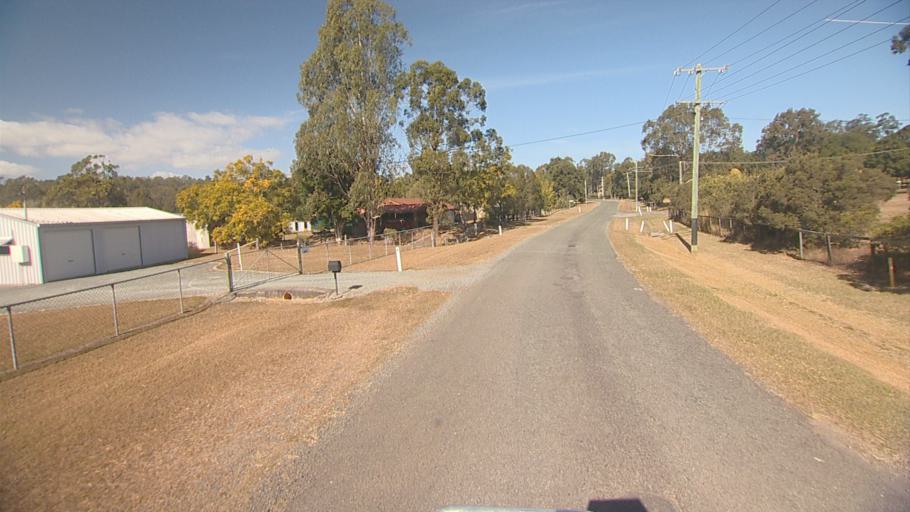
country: AU
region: Queensland
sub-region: Logan
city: Cedar Vale
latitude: -27.8559
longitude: 152.9764
